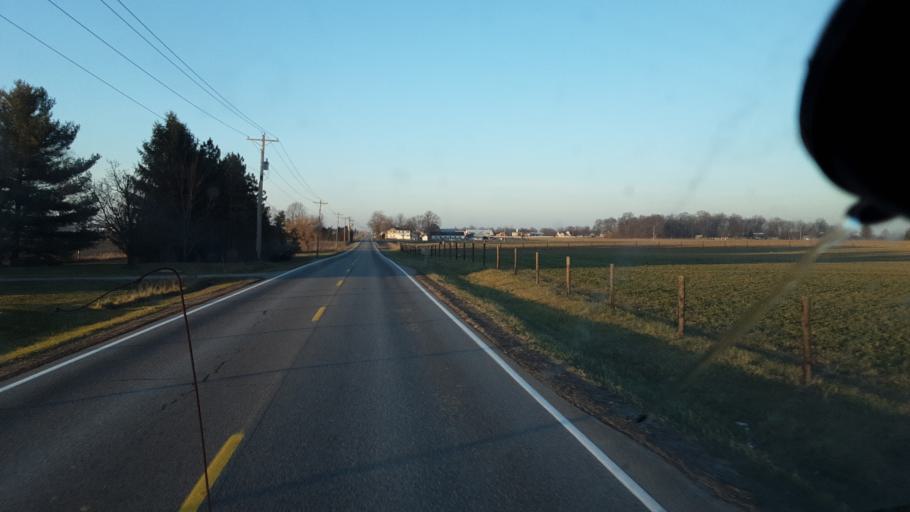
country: US
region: Indiana
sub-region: Allen County
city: Harlan
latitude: 41.1919
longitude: -84.9412
